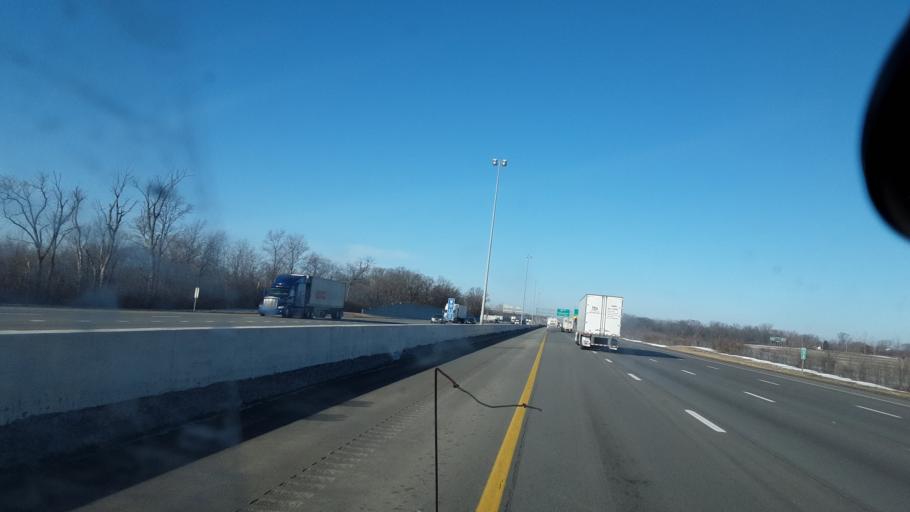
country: US
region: Ohio
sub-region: Montgomery County
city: Vandalia
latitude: 39.8644
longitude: -84.2047
